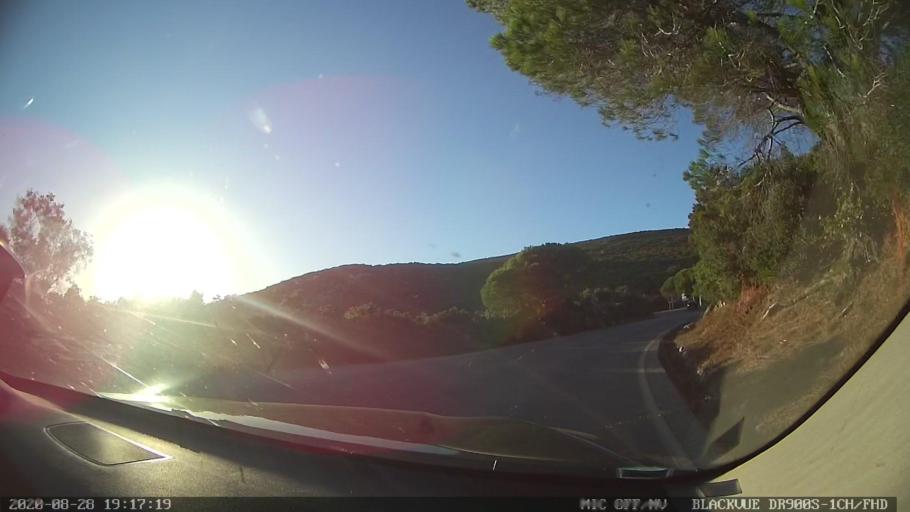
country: PT
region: Setubal
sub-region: Sesimbra
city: Sesimbra
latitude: 38.4598
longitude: -9.0104
